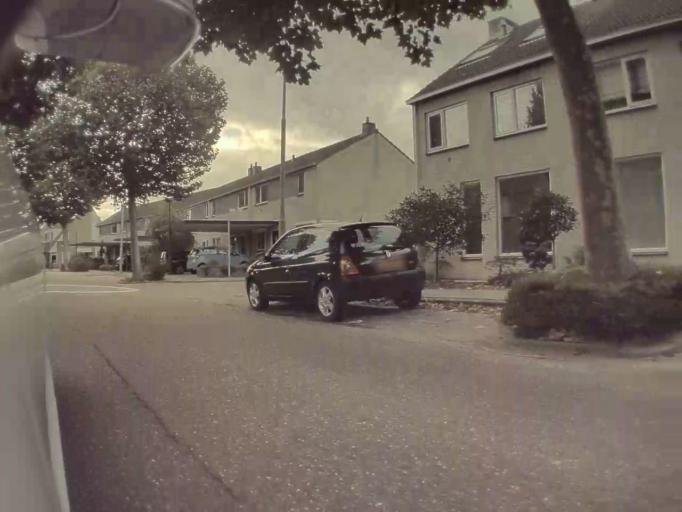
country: NL
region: Zeeland
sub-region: Gemeente Middelburg
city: Middelburg
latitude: 51.4836
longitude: 3.6090
